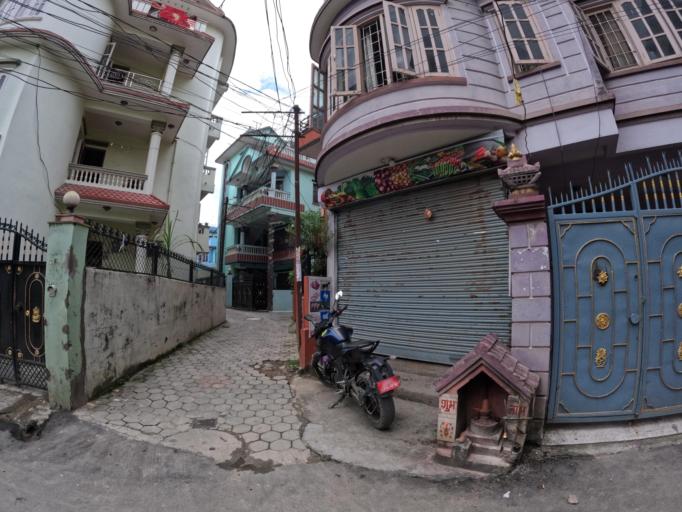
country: NP
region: Central Region
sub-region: Bagmati Zone
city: Kathmandu
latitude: 27.7424
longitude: 85.3214
